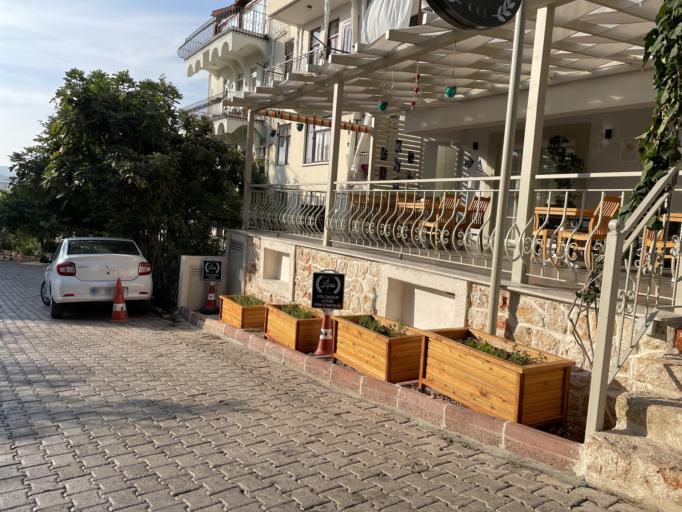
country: TR
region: Antalya
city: Kas
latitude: 36.1994
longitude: 29.6439
